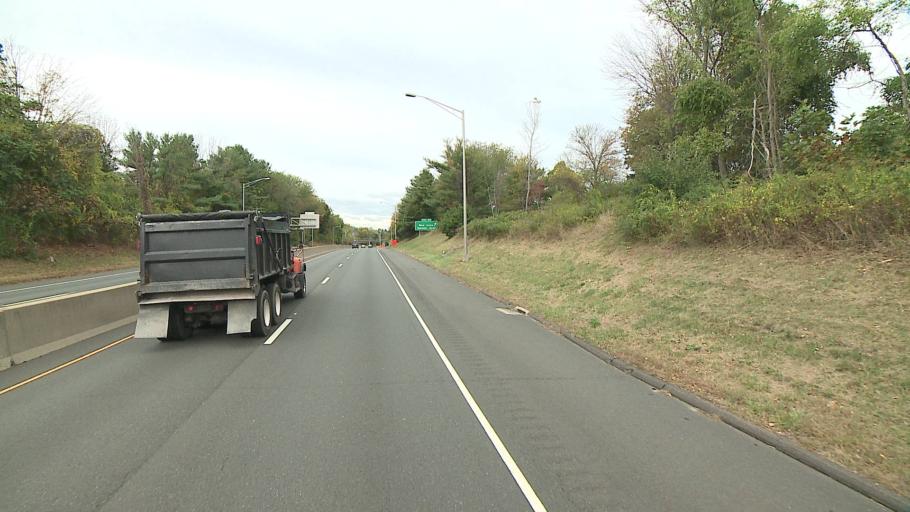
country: US
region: Connecticut
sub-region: Middlesex County
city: Middletown
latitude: 41.5437
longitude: -72.6278
